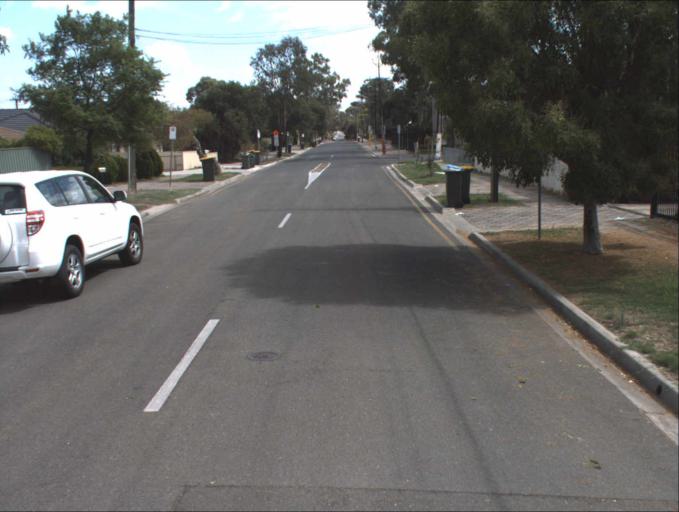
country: AU
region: South Australia
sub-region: Port Adelaide Enfield
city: Gilles Plains
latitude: -34.8630
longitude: 138.6577
